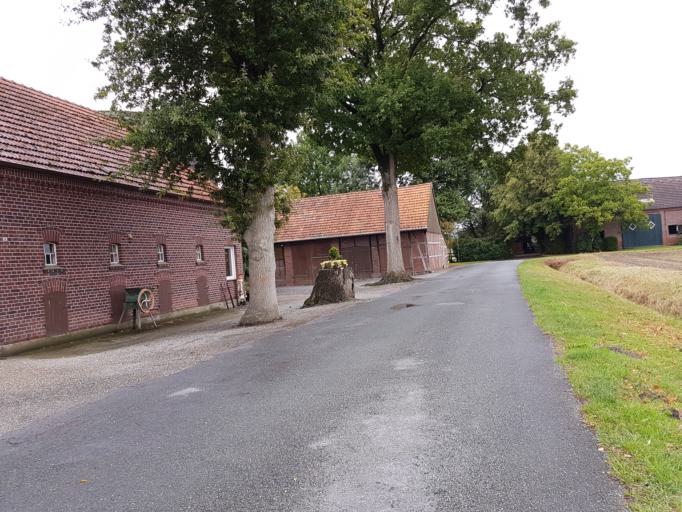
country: DE
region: North Rhine-Westphalia
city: Olfen
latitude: 51.7257
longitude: 7.3822
